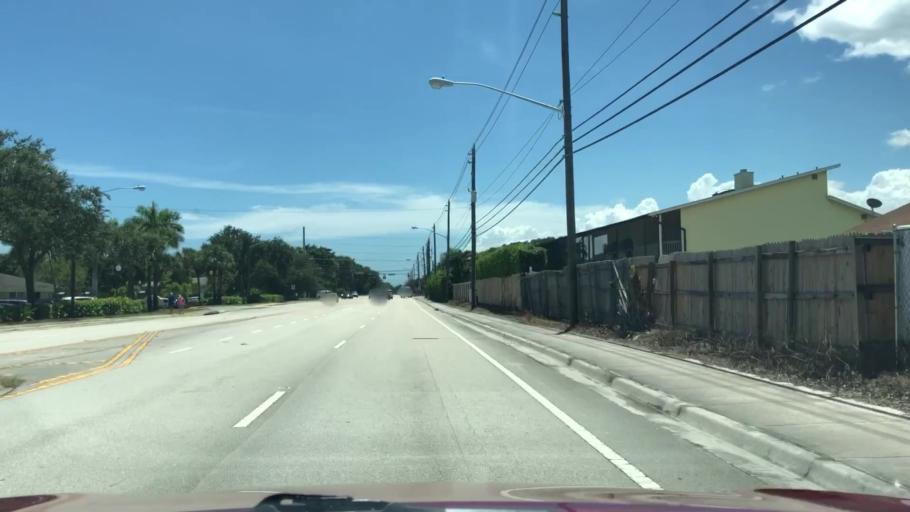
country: US
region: Florida
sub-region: Palm Beach County
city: Boynton Beach
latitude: 26.5338
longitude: -80.1067
